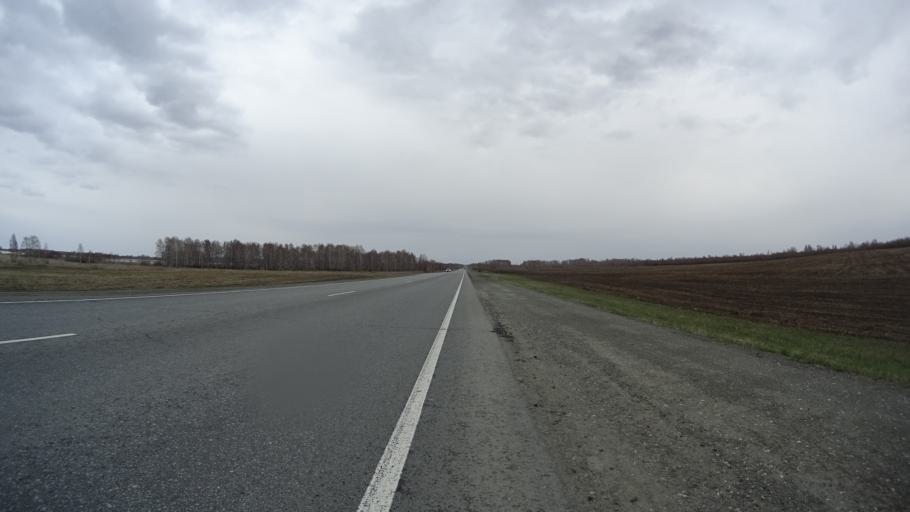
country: RU
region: Chelyabinsk
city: Krasnogorskiy
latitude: 54.6623
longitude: 61.2543
